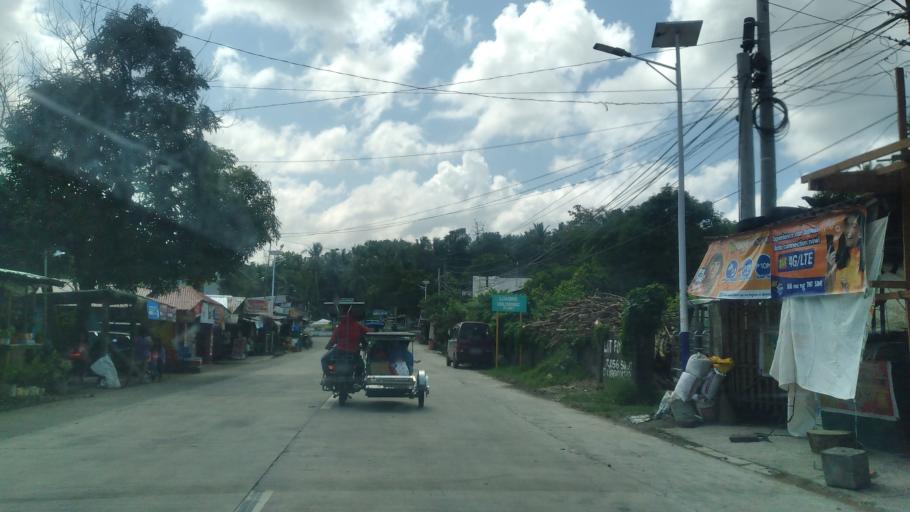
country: PH
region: Calabarzon
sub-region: Province of Quezon
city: Macalelon
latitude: 13.7563
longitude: 122.1437
